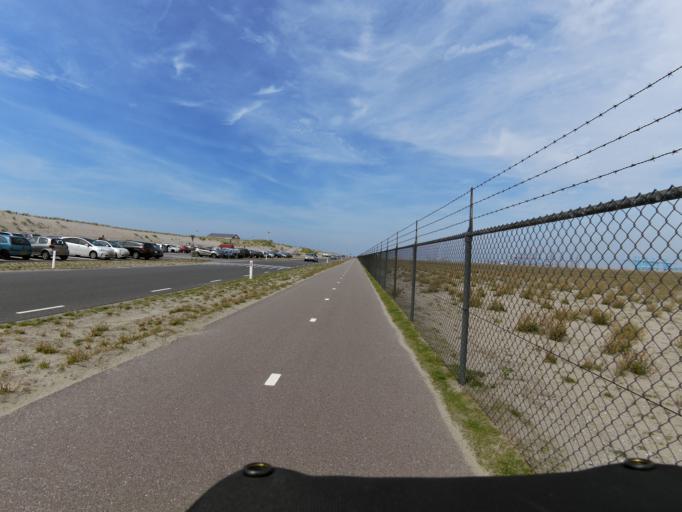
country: NL
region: South Holland
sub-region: Gemeente Goeree-Overflakkee
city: Goedereede
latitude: 51.9254
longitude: 3.9840
